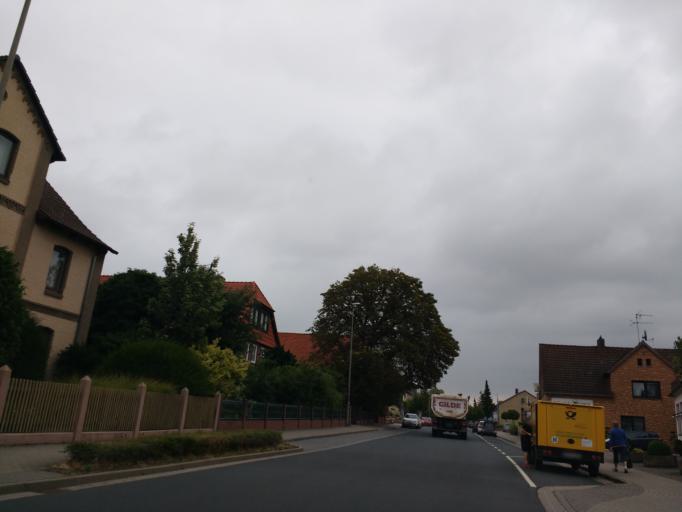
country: DE
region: Lower Saxony
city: Sohlde
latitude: 52.2088
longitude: 10.1826
